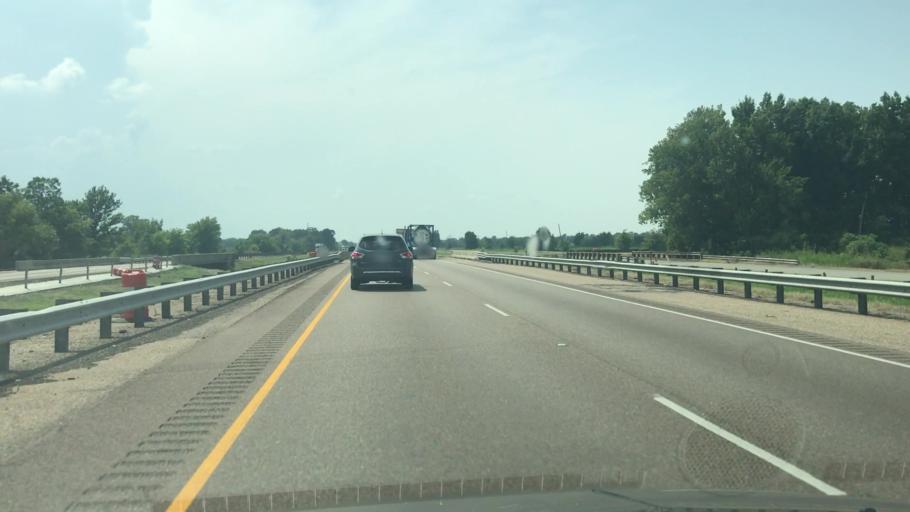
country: US
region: Arkansas
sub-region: Crittenden County
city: West Memphis
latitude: 35.1487
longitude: -90.3363
